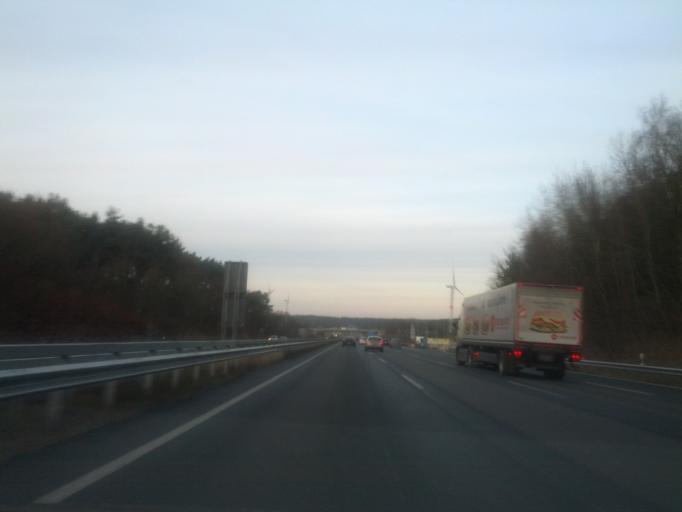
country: DE
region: Lower Saxony
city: Marxen
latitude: 53.3446
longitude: 10.0386
